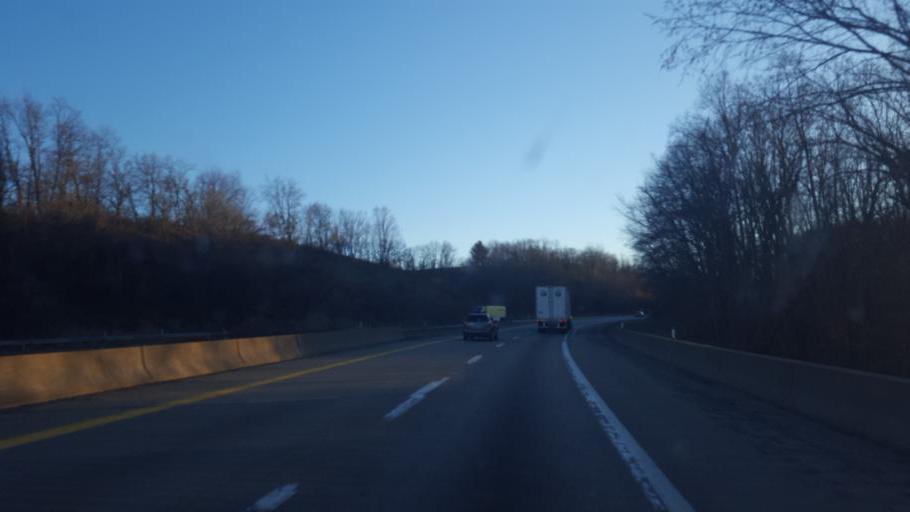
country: US
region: West Virginia
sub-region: Brooke County
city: Bethany
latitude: 40.1087
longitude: -80.4922
